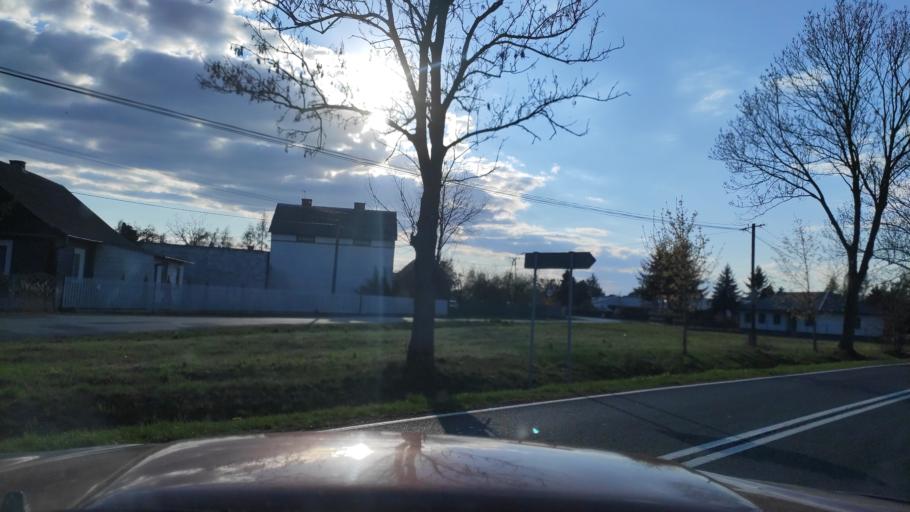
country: PL
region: Masovian Voivodeship
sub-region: Powiat zwolenski
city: Zwolen
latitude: 51.3832
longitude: 21.5577
